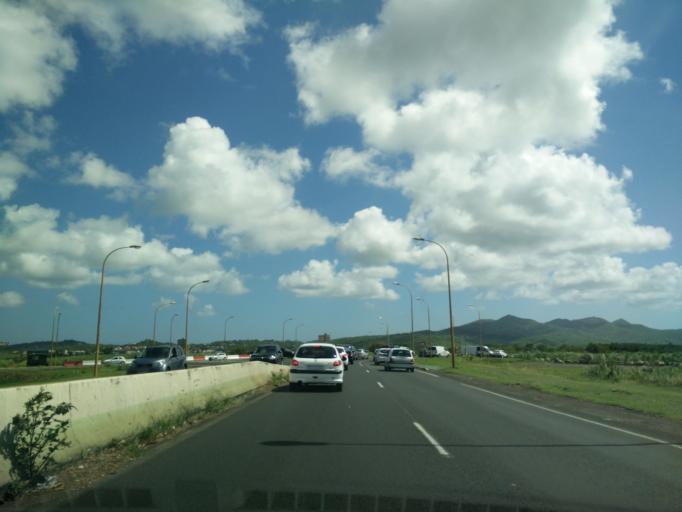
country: MQ
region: Martinique
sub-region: Martinique
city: Ducos
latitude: 14.5464
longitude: -60.9745
